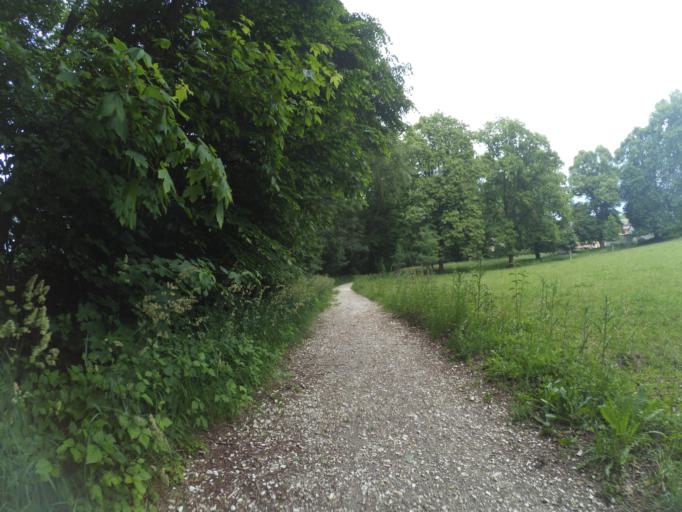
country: DE
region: Bavaria
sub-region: Swabia
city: Guenzburg
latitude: 48.4635
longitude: 10.2934
